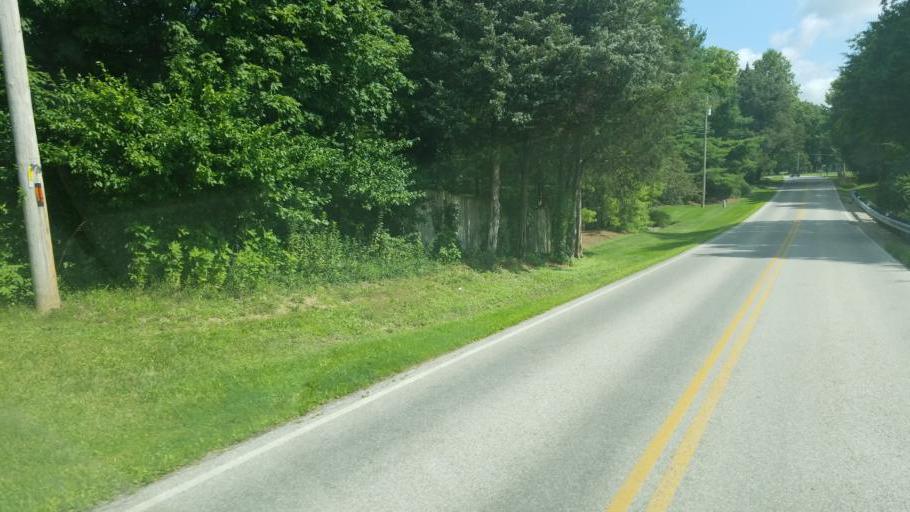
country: US
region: Ohio
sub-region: Delaware County
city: Sunbury
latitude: 40.2787
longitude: -82.9368
